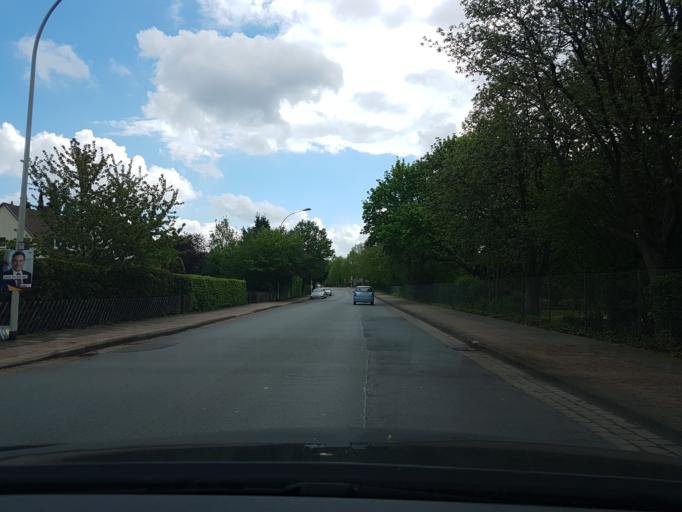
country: DE
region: Lower Saxony
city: Hameln
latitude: 52.1174
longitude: 9.3645
